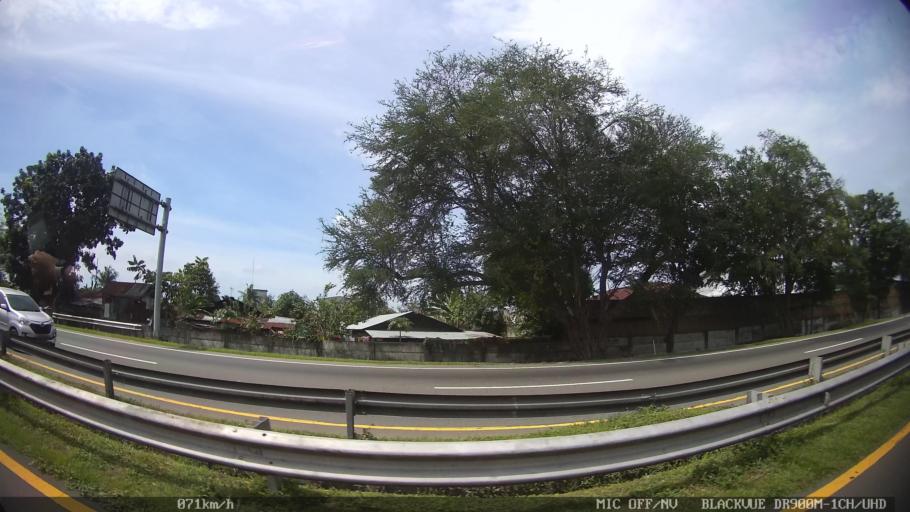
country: ID
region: North Sumatra
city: Medan
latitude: 3.6458
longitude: 98.6873
